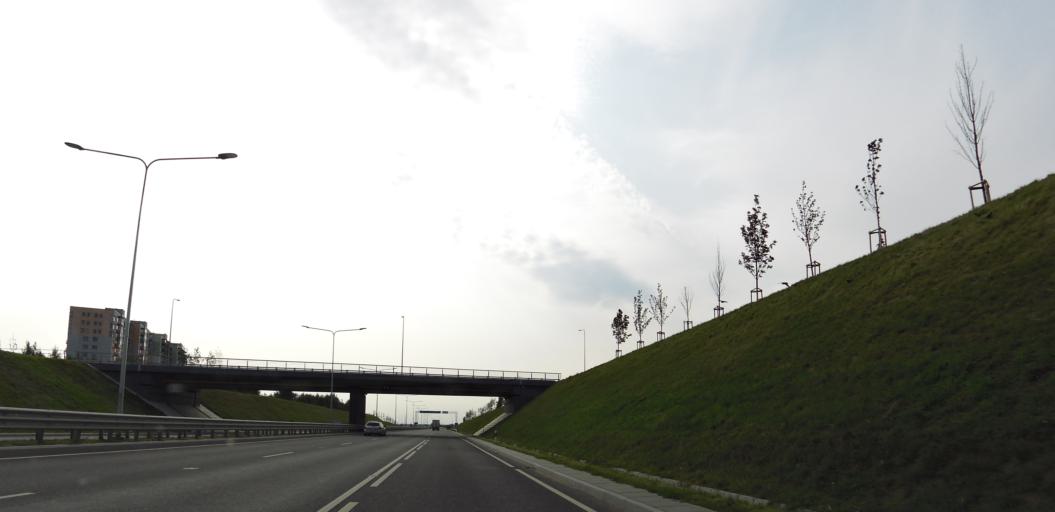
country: LT
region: Vilnius County
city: Pasilaiciai
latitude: 54.7402
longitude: 25.2140
